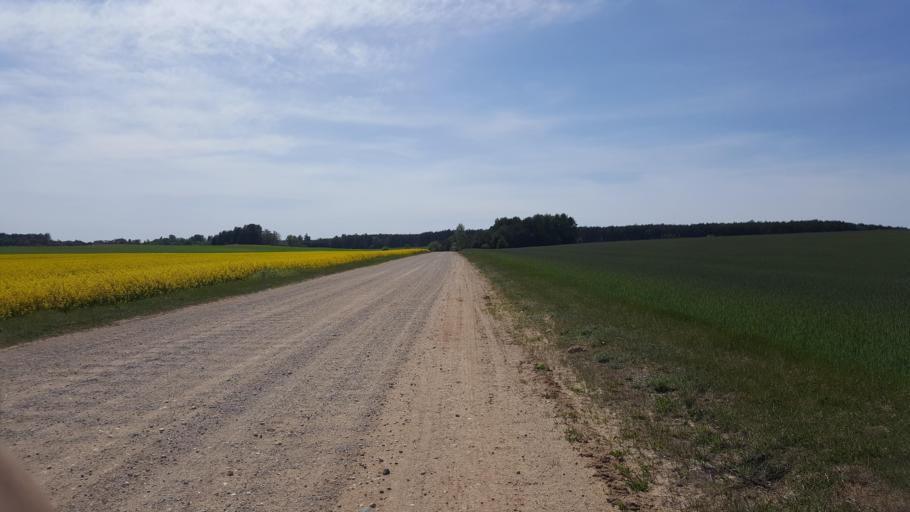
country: BY
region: Brest
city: Zhabinka
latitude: 52.3438
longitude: 24.1160
